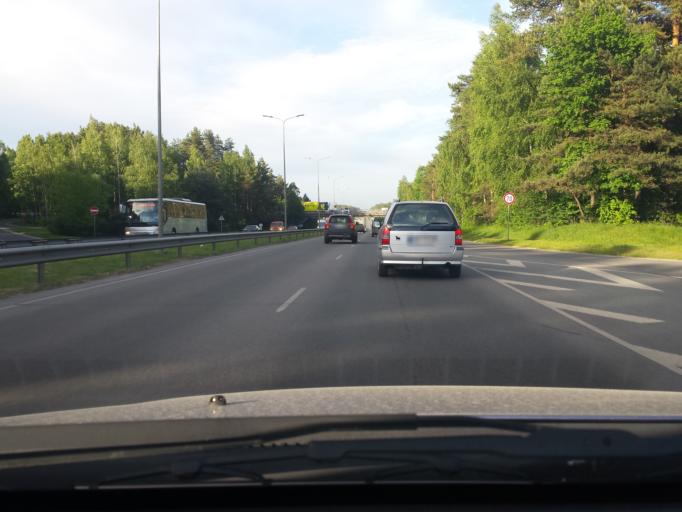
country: LV
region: Riga
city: Bergi
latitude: 56.9997
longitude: 24.2758
